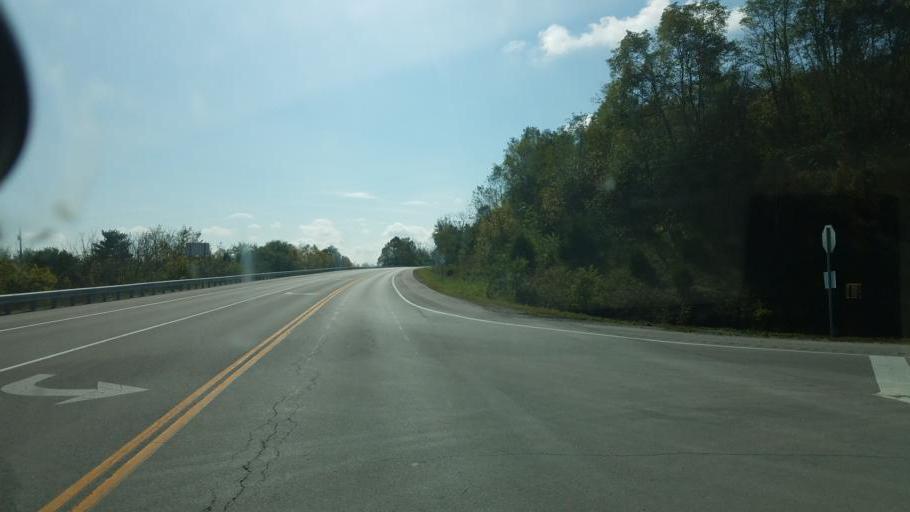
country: US
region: Ohio
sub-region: Brown County
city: Aberdeen
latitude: 38.6827
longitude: -83.7857
